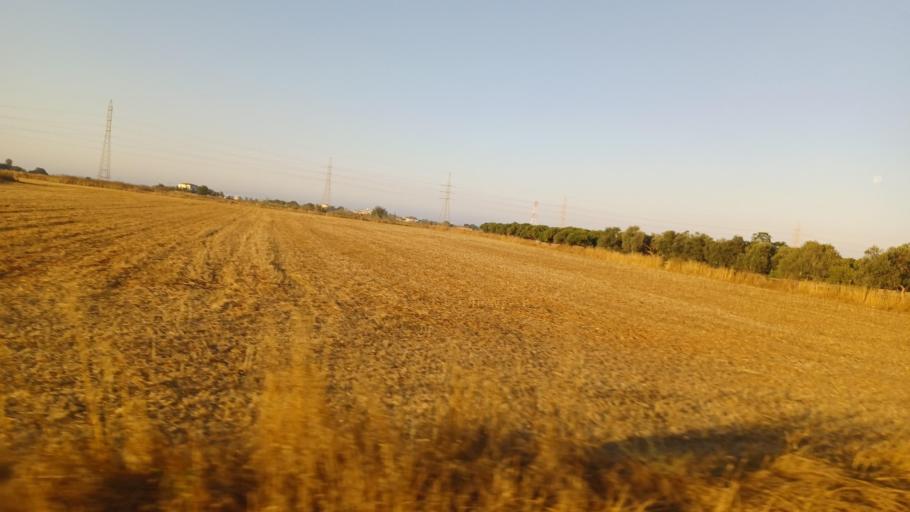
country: CY
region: Larnaka
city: Xylotymbou
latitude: 35.0048
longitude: 33.7875
